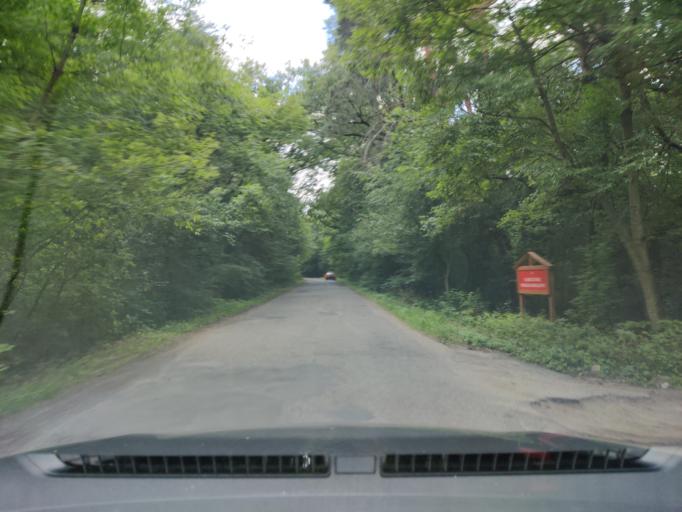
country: PL
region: Masovian Voivodeship
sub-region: Powiat pultuski
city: Pultusk
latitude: 52.7129
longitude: 21.1175
